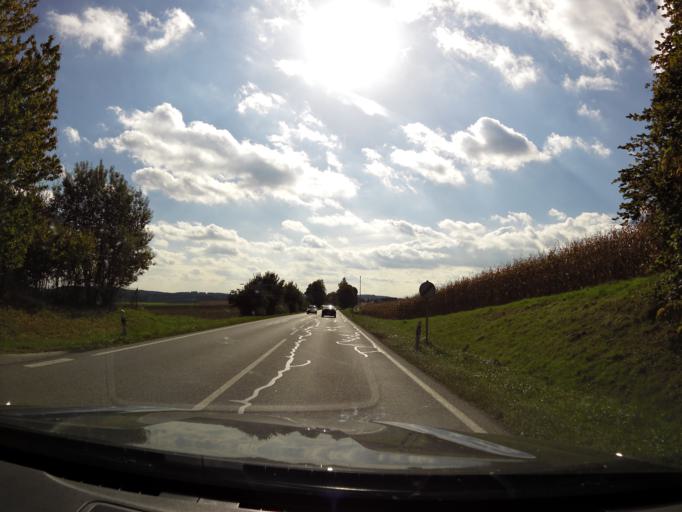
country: DE
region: Bavaria
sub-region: Lower Bavaria
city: Altfraunhofen
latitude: 48.4641
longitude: 12.1514
